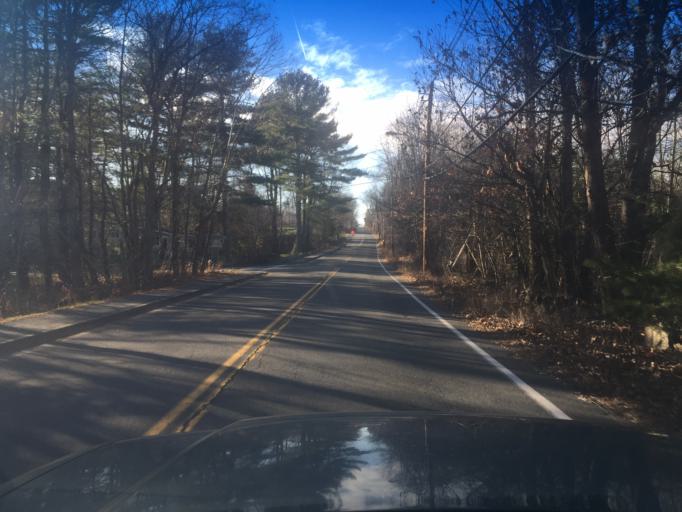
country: US
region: Massachusetts
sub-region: Middlesex County
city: Holliston
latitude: 42.2040
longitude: -71.4515
